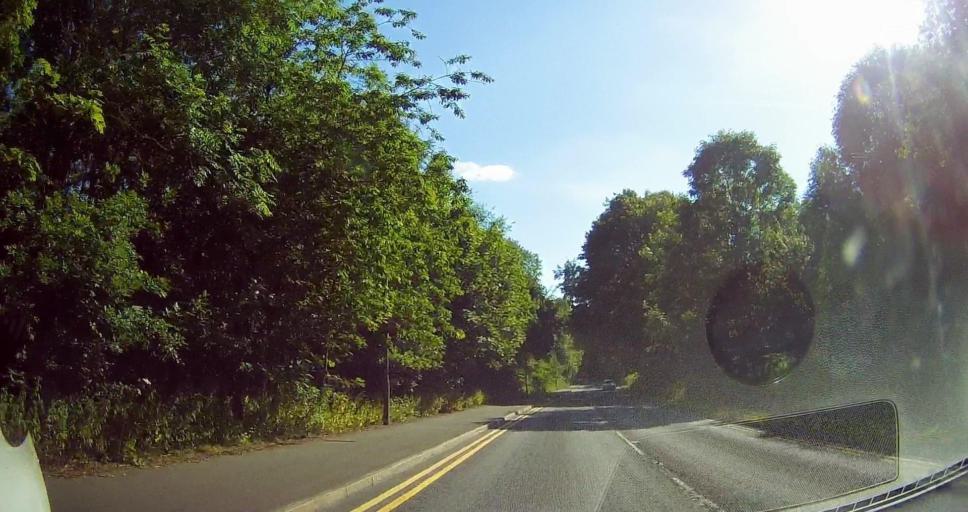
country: GB
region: England
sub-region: Cheshire East
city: Sandbach
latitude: 53.1466
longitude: -2.3532
